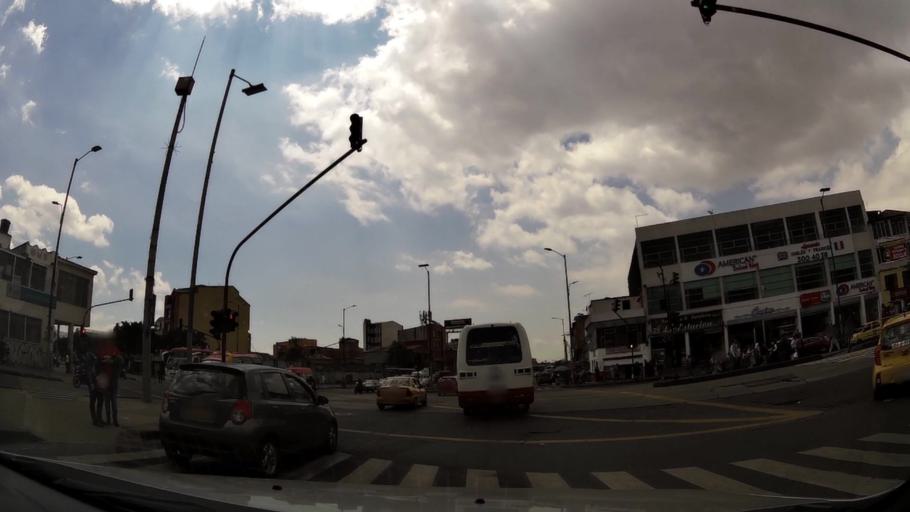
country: CO
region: Bogota D.C.
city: Bogota
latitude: 4.5812
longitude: -74.1023
